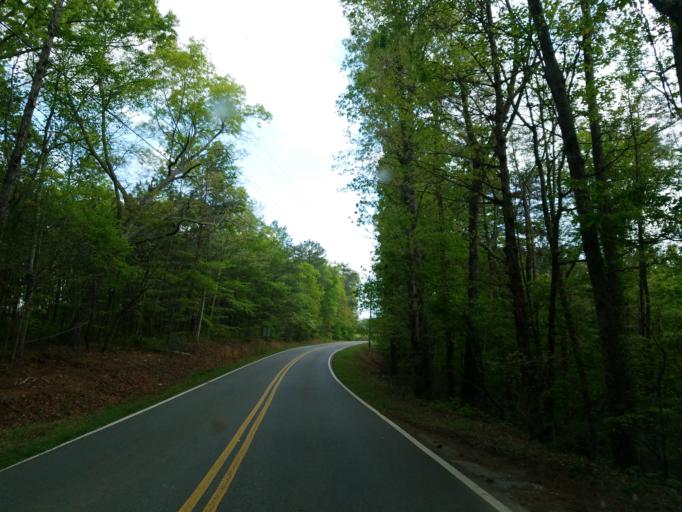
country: US
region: Georgia
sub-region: Pickens County
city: Jasper
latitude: 34.4325
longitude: -84.4589
